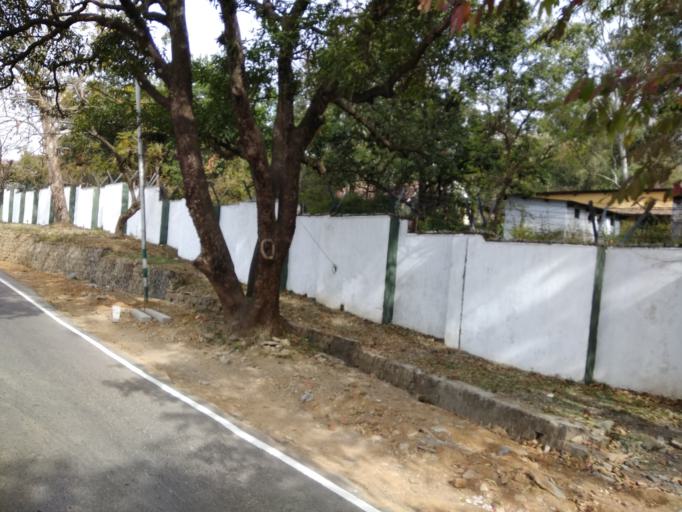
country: IN
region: Himachal Pradesh
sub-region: Kangra
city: Dharmsala
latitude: 32.1737
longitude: 76.3849
